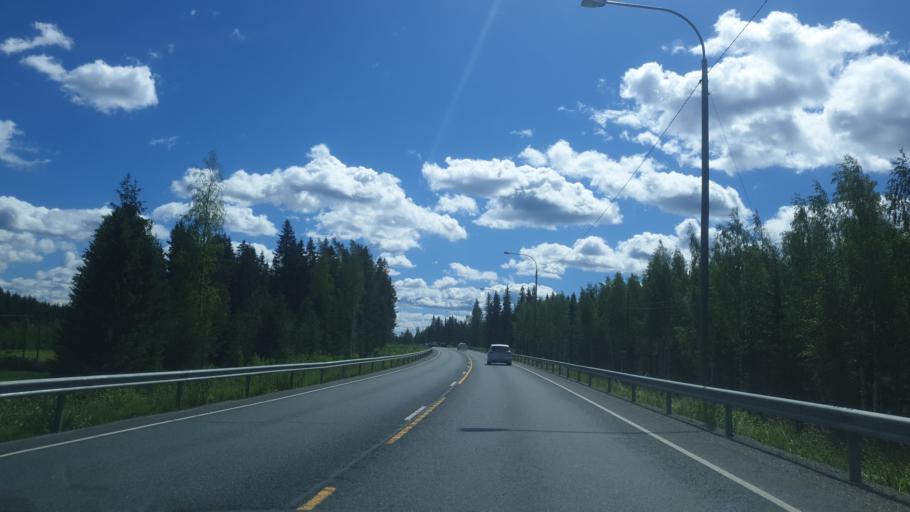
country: FI
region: Northern Savo
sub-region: Varkaus
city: Leppaevirta
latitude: 62.5455
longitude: 27.6250
